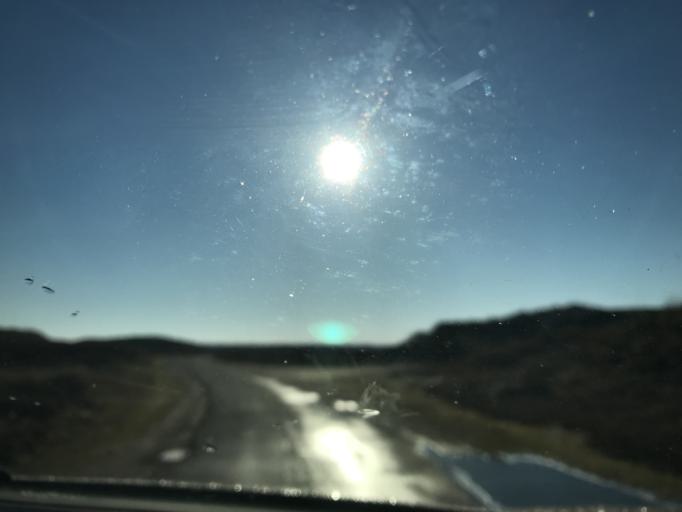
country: DK
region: Central Jutland
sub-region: Ringkobing-Skjern Kommune
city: Hvide Sande
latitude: 55.8135
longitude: 8.1765
